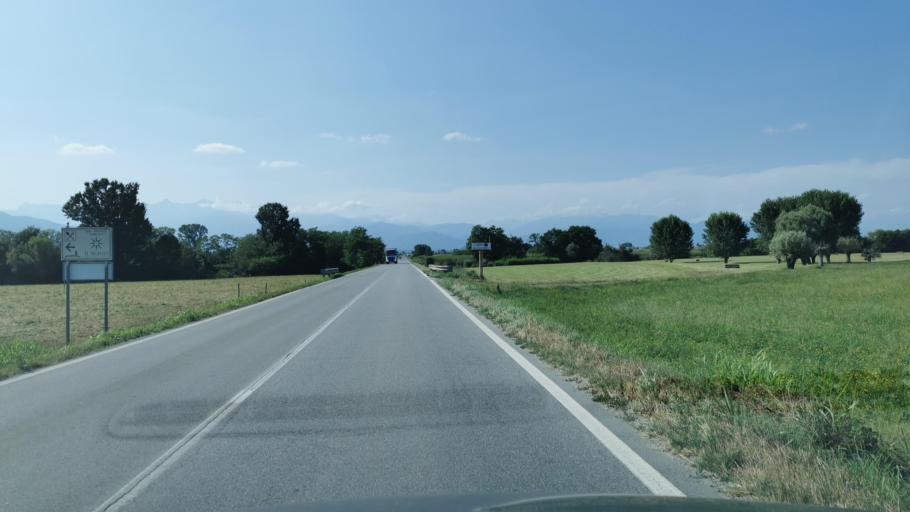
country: IT
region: Piedmont
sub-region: Provincia di Cuneo
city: Carde
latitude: 44.7235
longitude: 7.4366
